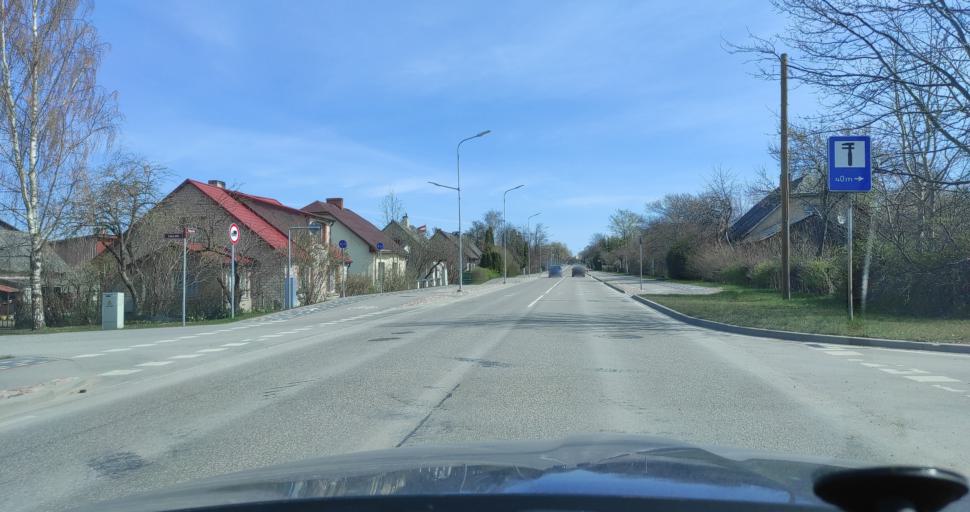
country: LV
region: Talsu Rajons
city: Talsi
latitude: 57.2382
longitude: 22.5729
